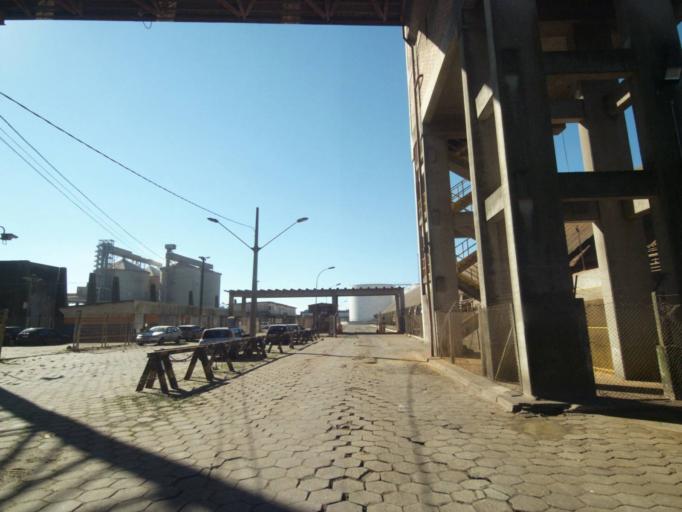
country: BR
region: Parana
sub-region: Paranagua
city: Paranagua
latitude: -25.5059
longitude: -48.5072
